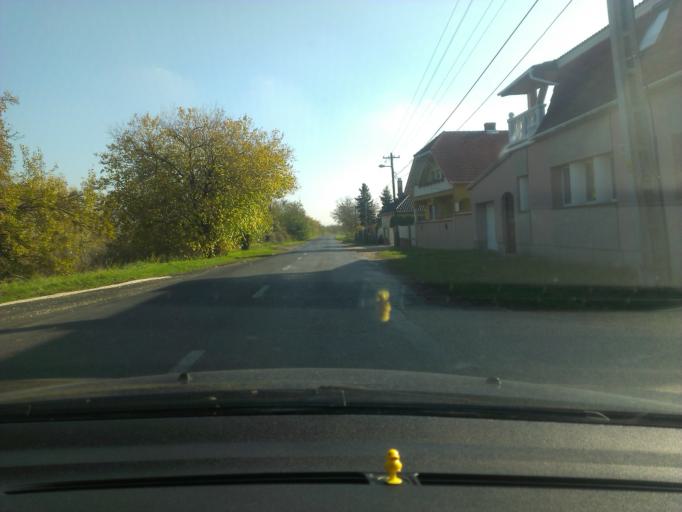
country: HU
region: Komarom-Esztergom
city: Komarom
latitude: 47.7233
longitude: 18.1675
